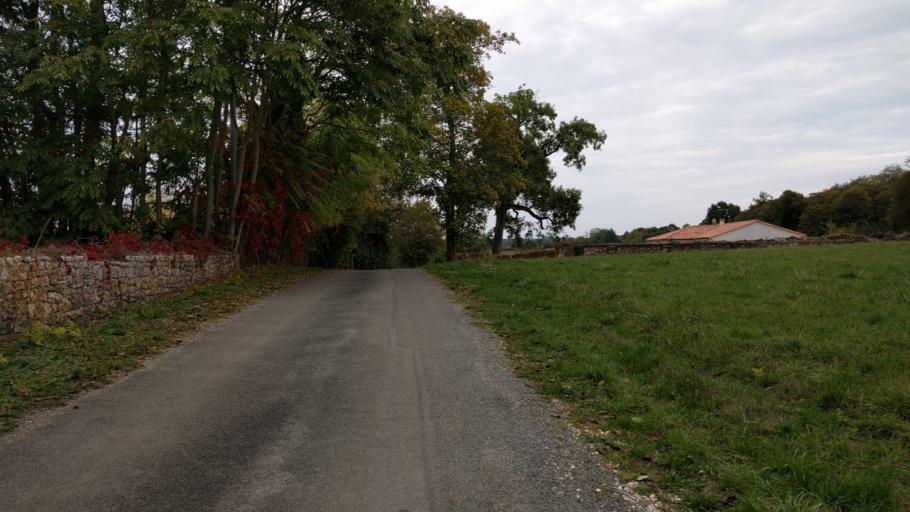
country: FR
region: Aquitaine
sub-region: Departement de la Dordogne
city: Mouleydier
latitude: 44.8963
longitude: 0.6496
